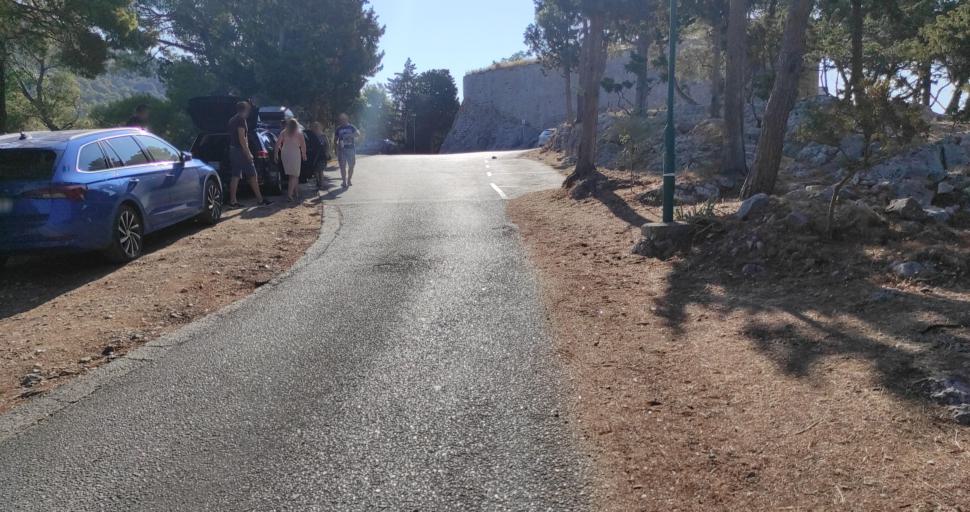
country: HR
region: Splitsko-Dalmatinska
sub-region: Grad Hvar
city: Hvar
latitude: 43.1752
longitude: 16.4408
